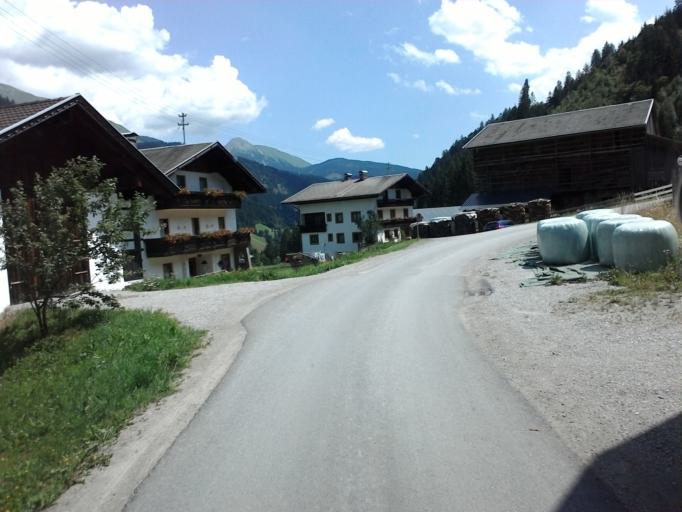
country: AT
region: Tyrol
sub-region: Politischer Bezirk Lienz
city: Untertilliach
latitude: 46.6992
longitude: 12.7498
